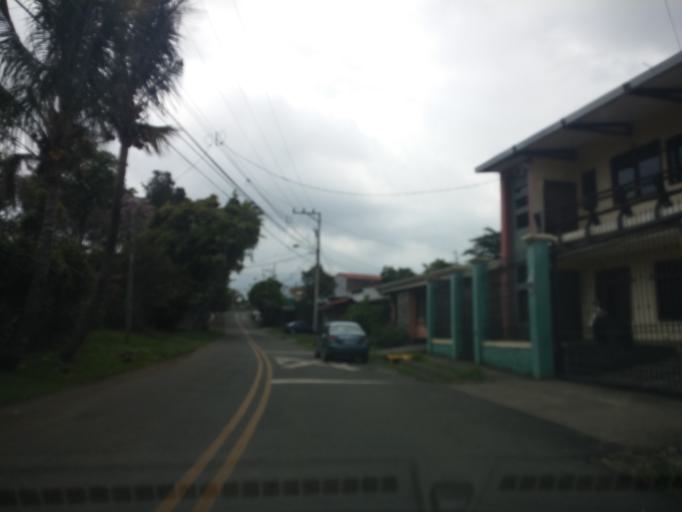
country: CR
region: Heredia
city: Llorente
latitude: 10.0018
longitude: -84.1474
